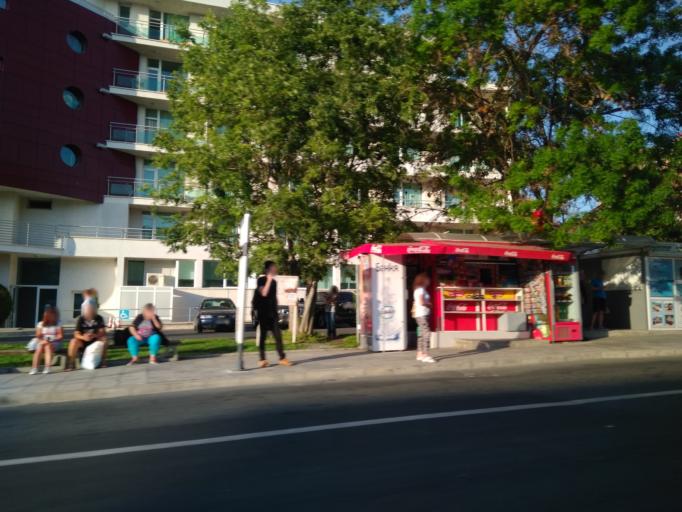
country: BG
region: Burgas
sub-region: Obshtina Nesebur
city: Nesebar
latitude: 42.6643
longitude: 27.7164
